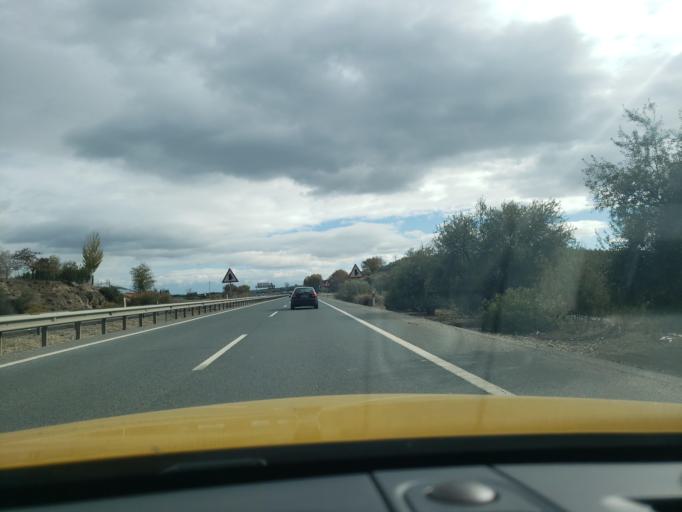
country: ES
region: Andalusia
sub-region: Provincia de Granada
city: Lachar
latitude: 37.1915
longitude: -3.8375
